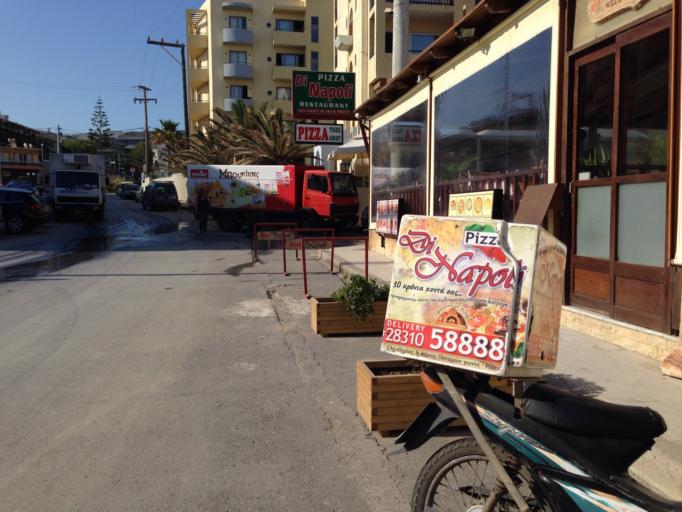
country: GR
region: Crete
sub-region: Nomos Rethymnis
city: Rethymno
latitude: 35.3667
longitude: 24.4916
